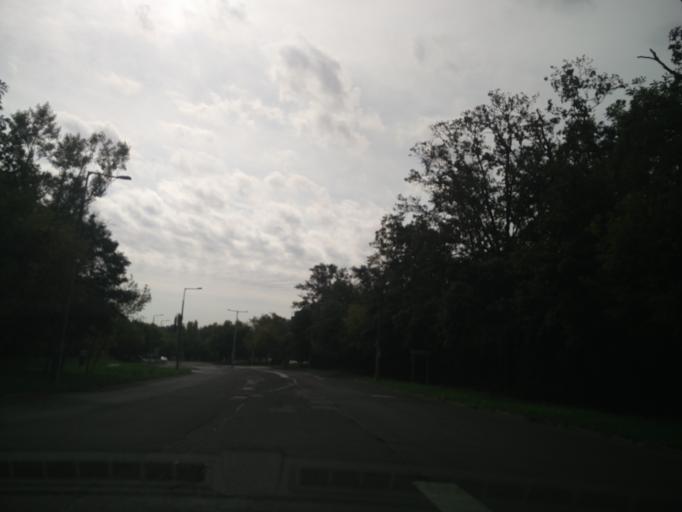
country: HU
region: Budapest
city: Budapest XV. keruelet
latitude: 47.5830
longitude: 19.1047
